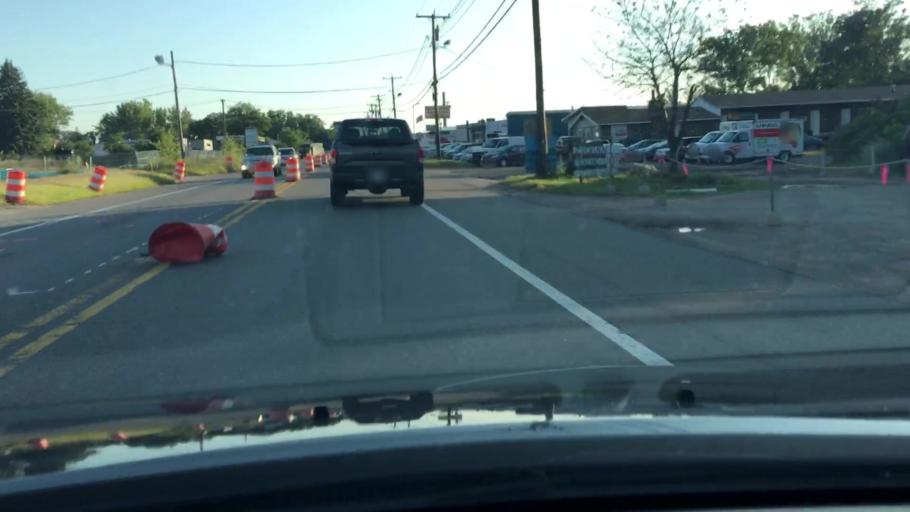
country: US
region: Massachusetts
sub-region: Worcester County
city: Sunderland
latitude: 42.2325
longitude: -71.7519
